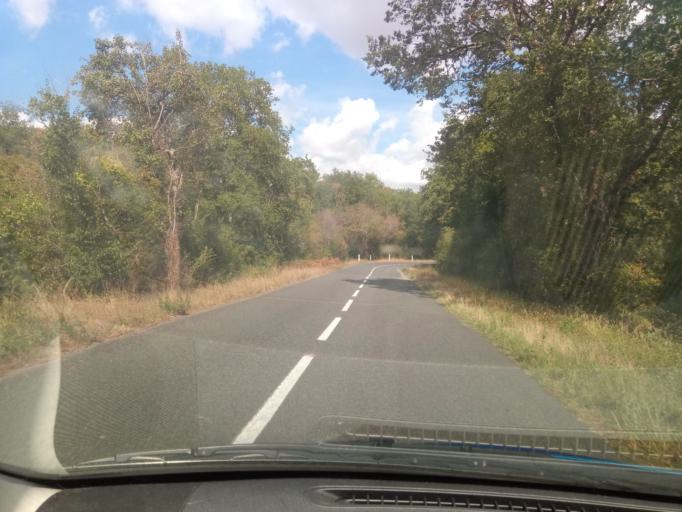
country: FR
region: Poitou-Charentes
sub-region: Departement de la Vienne
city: Saint-Savin
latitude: 46.5152
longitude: 0.8316
